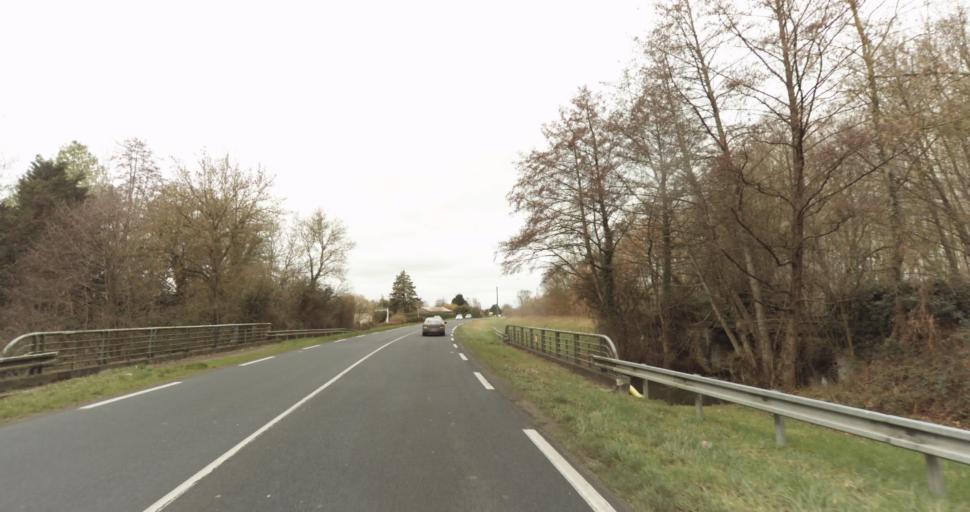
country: FR
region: Pays de la Loire
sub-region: Departement de Maine-et-Loire
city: Jumelles
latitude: 47.3838
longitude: -0.1113
